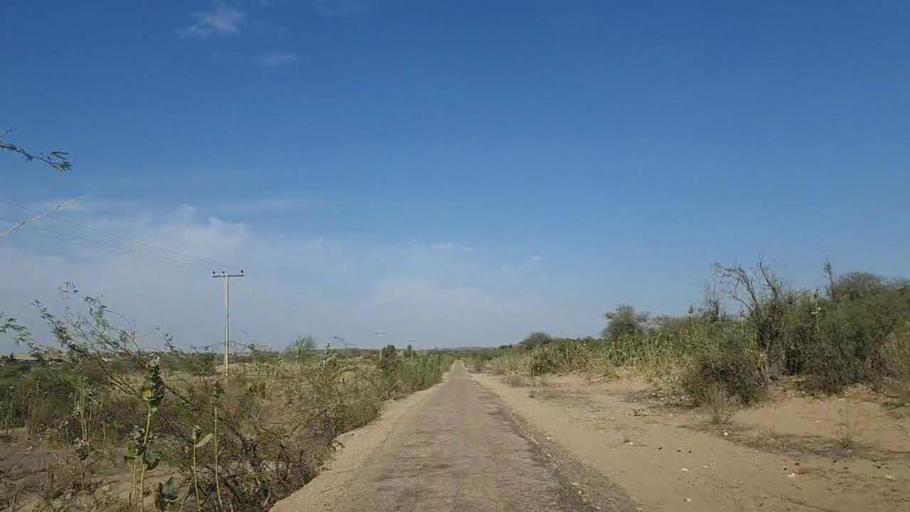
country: PK
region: Sindh
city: Naukot
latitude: 24.8271
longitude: 69.5446
